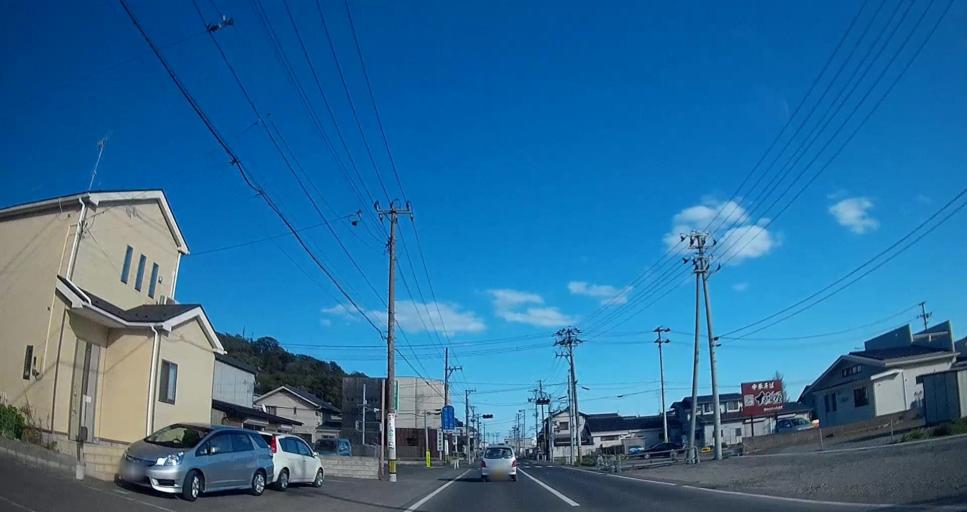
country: JP
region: Miyagi
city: Ishinomaki
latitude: 38.4232
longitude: 141.3195
